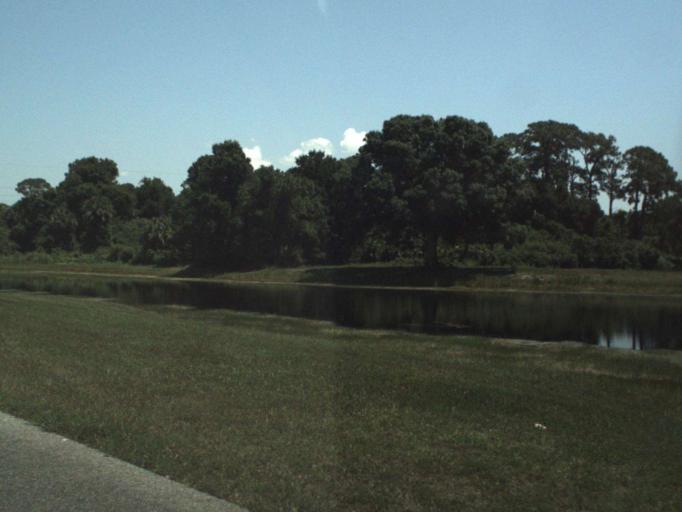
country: US
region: Florida
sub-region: Brevard County
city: Cocoa
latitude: 28.4149
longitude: -80.7064
